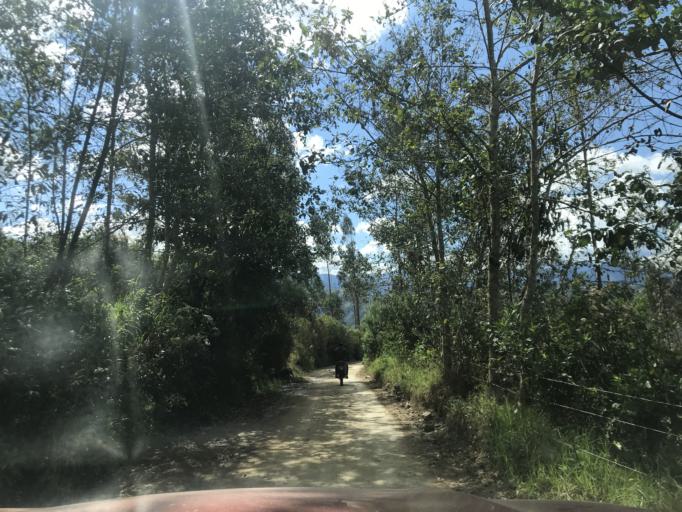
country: PE
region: Cajamarca
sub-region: Provincia de Chota
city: Querocoto
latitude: -6.3334
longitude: -79.0707
